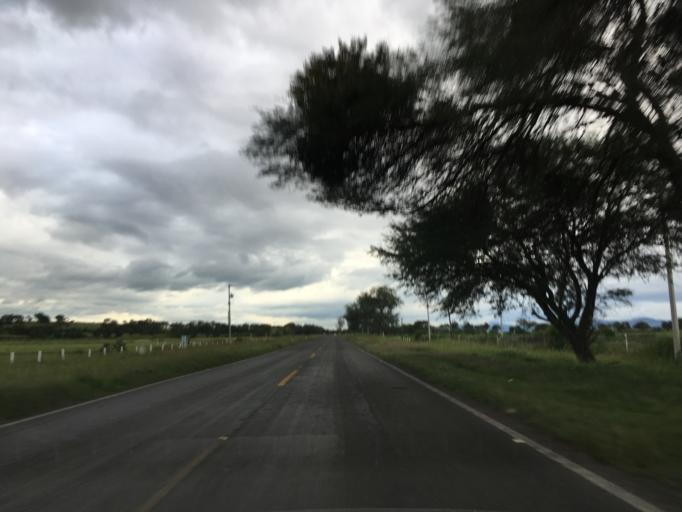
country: MX
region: Michoacan
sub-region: Cuitzeo
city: Cuamio
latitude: 20.0078
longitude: -101.1553
